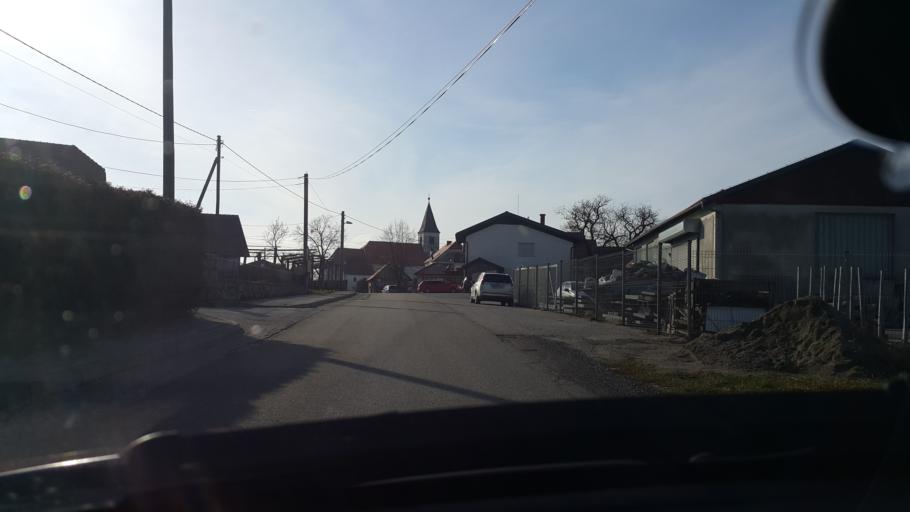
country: SI
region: Slovenska Bistrica
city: Zgornja Polskava
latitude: 46.4271
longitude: 15.6259
